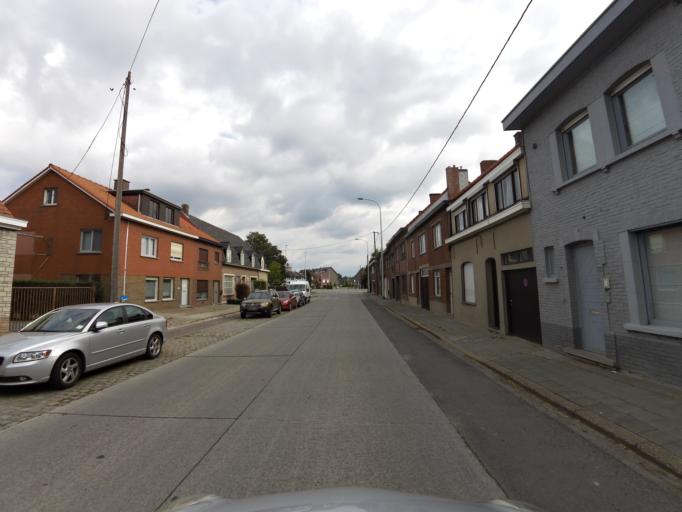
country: BE
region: Flanders
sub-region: Provincie West-Vlaanderen
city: Tielt
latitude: 50.9991
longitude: 3.3107
